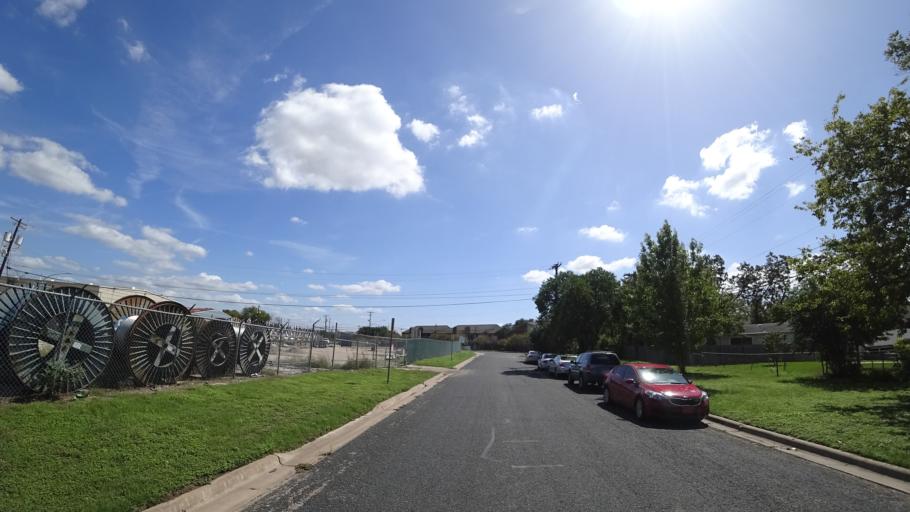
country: US
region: Texas
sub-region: Travis County
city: Austin
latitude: 30.3385
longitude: -97.7216
